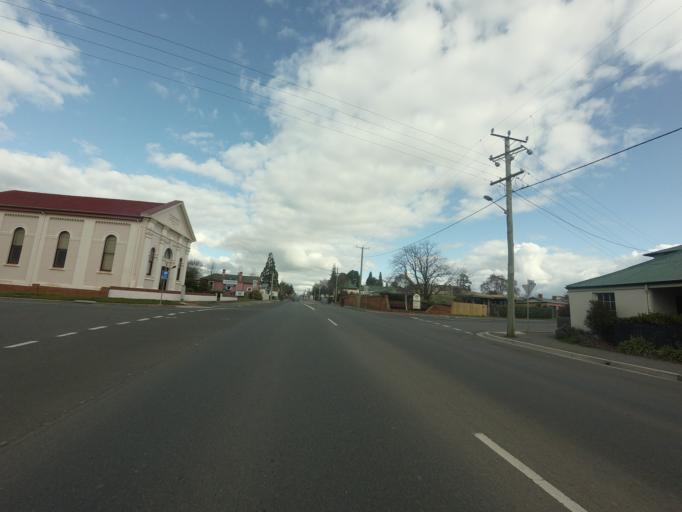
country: AU
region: Tasmania
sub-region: Northern Midlands
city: Longford
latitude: -41.5913
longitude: 147.1211
